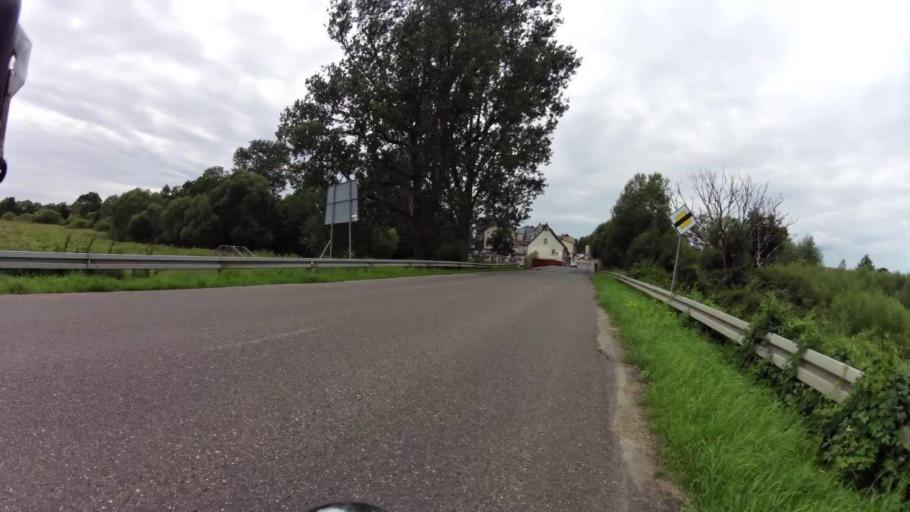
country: PL
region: West Pomeranian Voivodeship
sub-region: Powiat bialogardzki
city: Karlino
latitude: 54.0318
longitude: 15.8802
